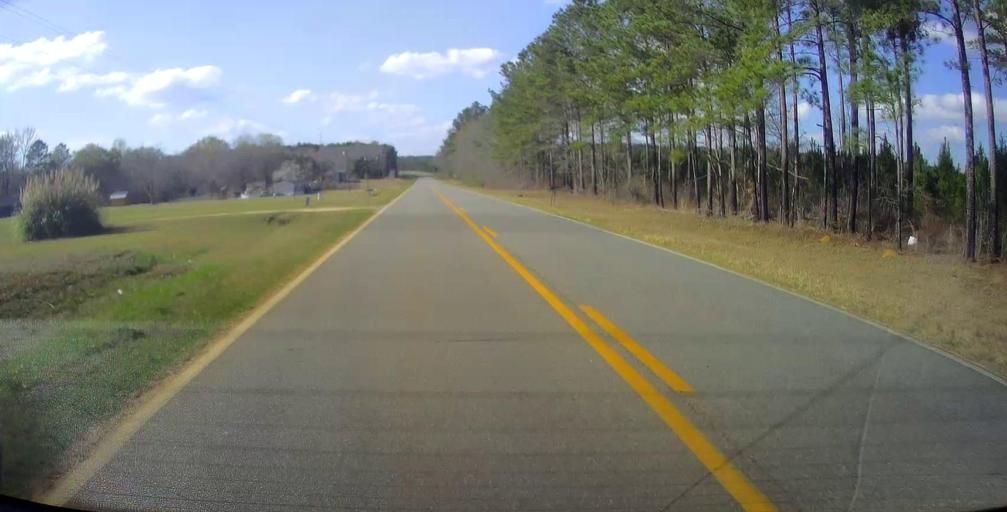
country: US
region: Georgia
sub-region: Laurens County
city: Dublin
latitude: 32.5803
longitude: -83.0520
